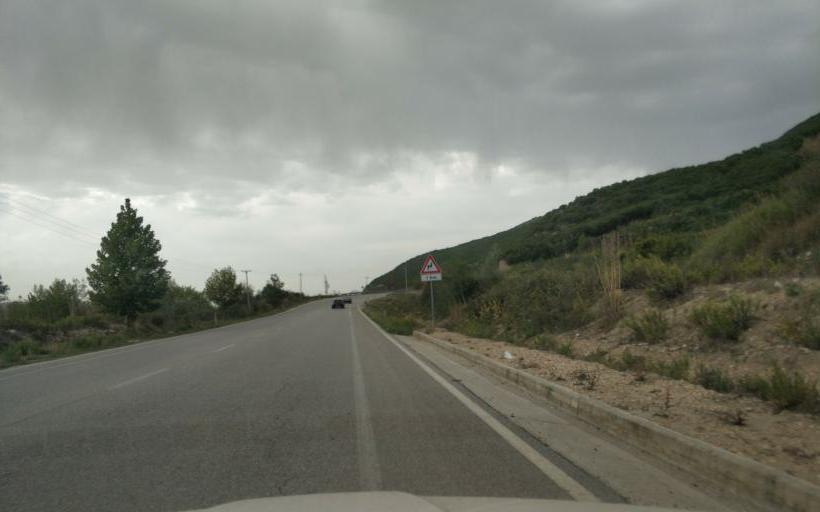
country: AL
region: Fier
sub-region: Rrethi i Mallakastres
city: Hekal
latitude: 40.5254
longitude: 19.7357
